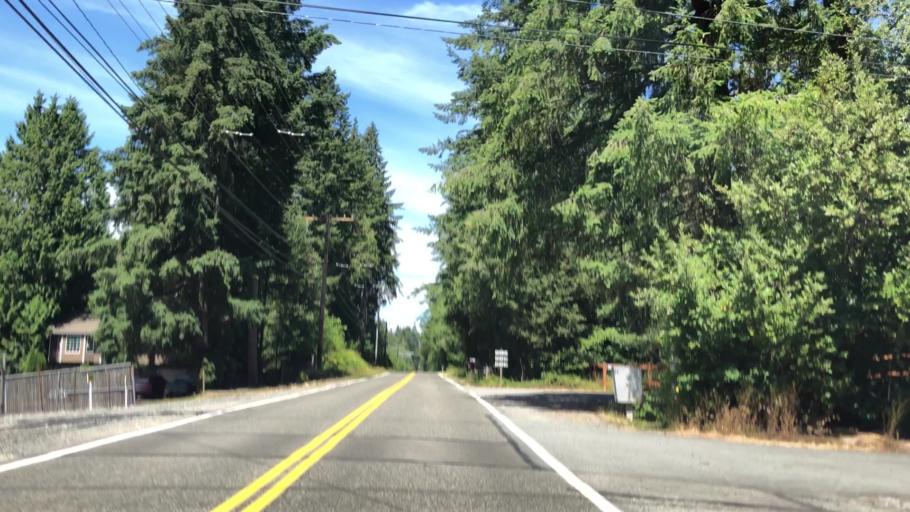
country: US
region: Washington
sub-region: Snohomish County
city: North Creek
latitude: 47.8304
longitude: -122.1642
